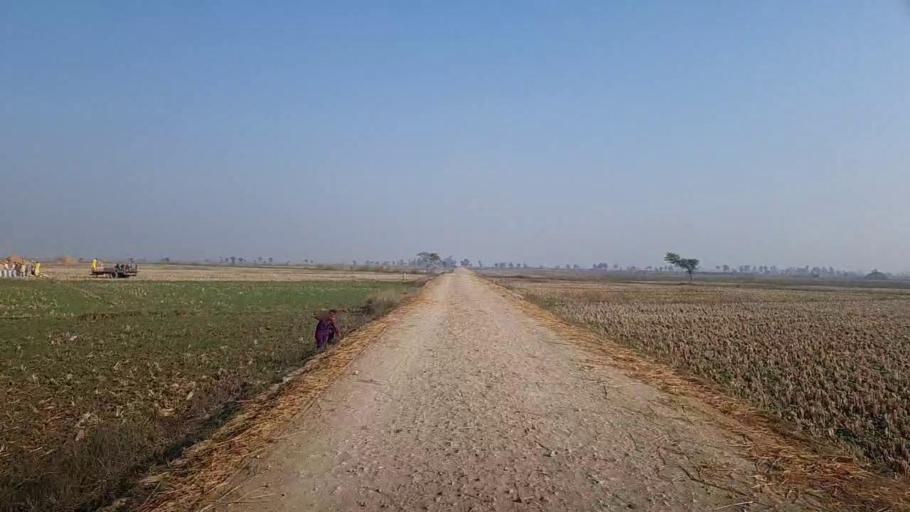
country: PK
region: Sindh
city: Radhan
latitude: 27.1220
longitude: 67.8980
